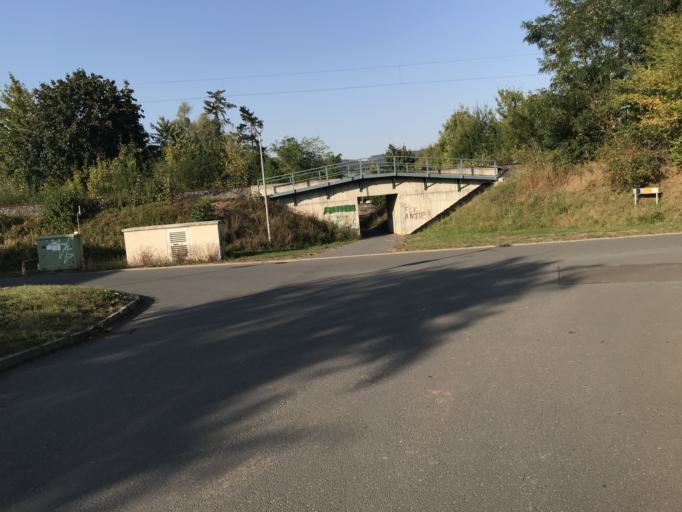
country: DE
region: Hesse
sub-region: Regierungsbezirk Kassel
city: Eschwege
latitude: 51.1927
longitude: 10.0287
